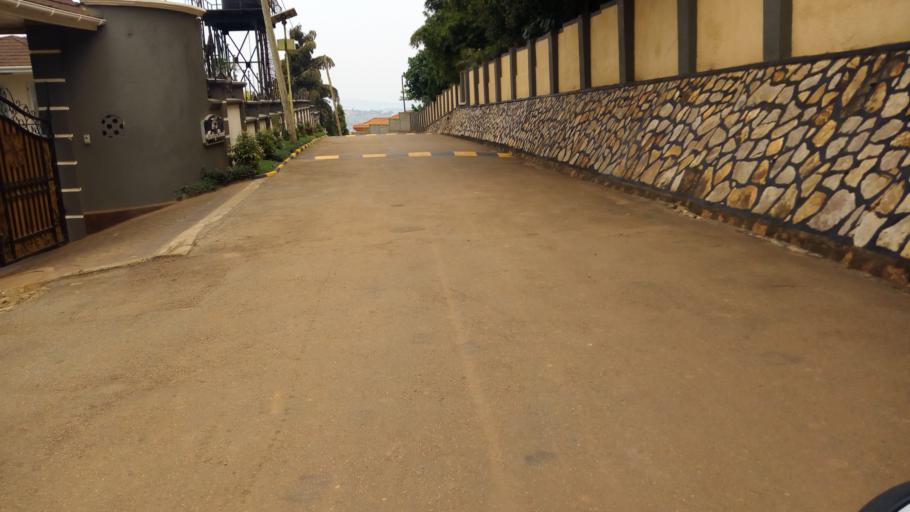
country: UG
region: Central Region
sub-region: Wakiso District
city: Kireka
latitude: 0.3268
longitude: 32.6333
